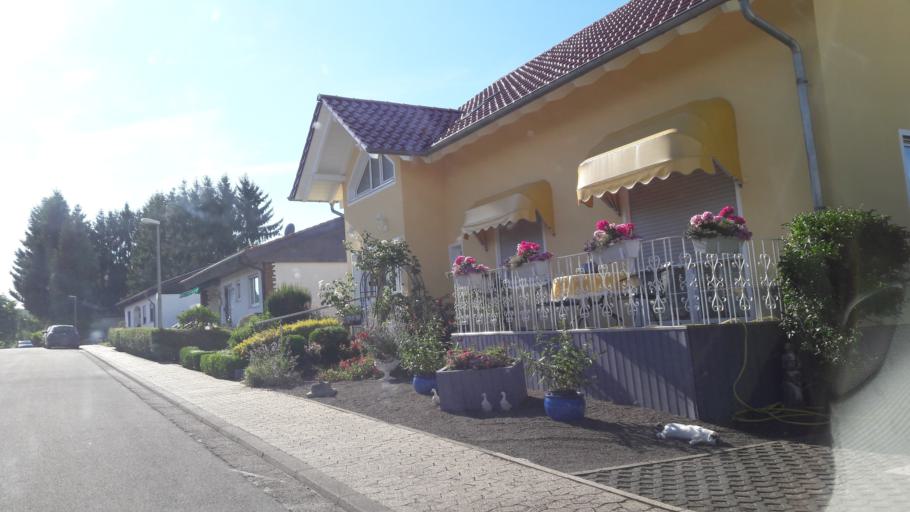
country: DE
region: Rheinland-Pfalz
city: Achtelsbach
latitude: 49.5742
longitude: 7.0520
